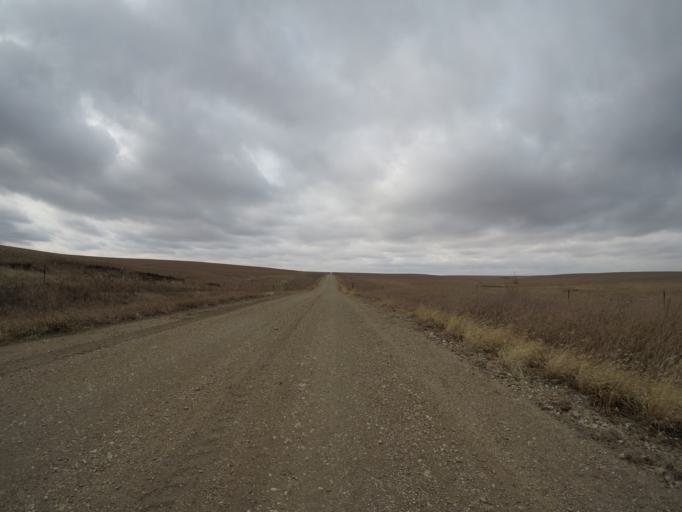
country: US
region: Kansas
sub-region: Morris County
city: Council Grove
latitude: 38.7245
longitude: -96.1962
